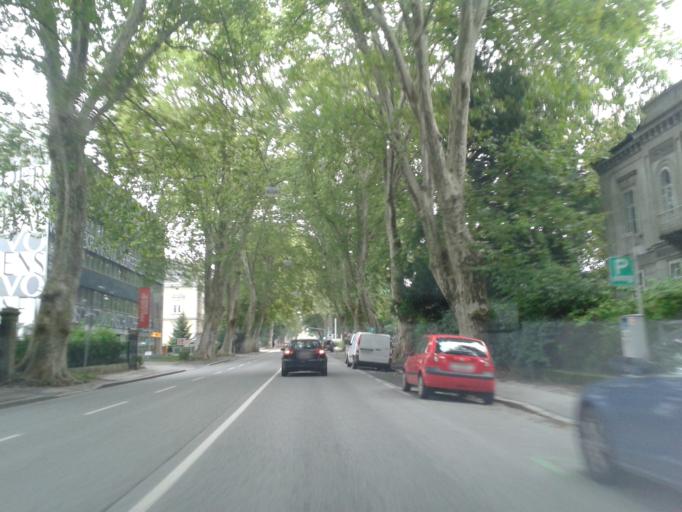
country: AT
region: Styria
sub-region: Graz Stadt
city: Graz
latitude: 47.0758
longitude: 15.4552
